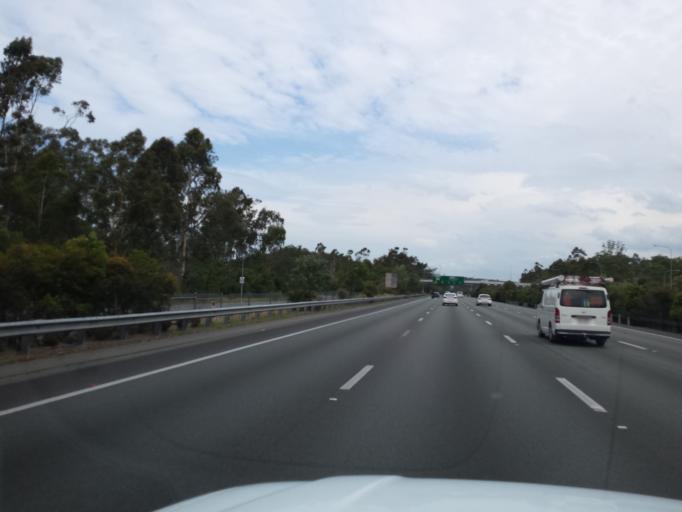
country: AU
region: Queensland
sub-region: Gold Coast
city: Nerang
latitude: -27.9477
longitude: 153.3409
